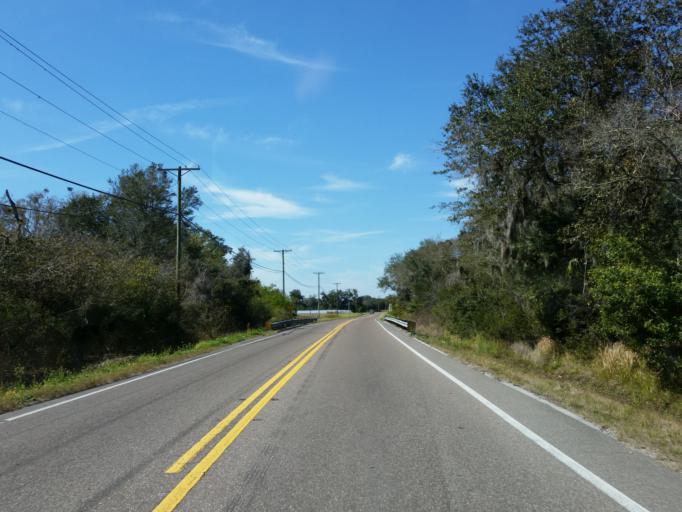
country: US
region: Florida
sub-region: Hillsborough County
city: Balm
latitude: 27.7629
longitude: -82.2605
